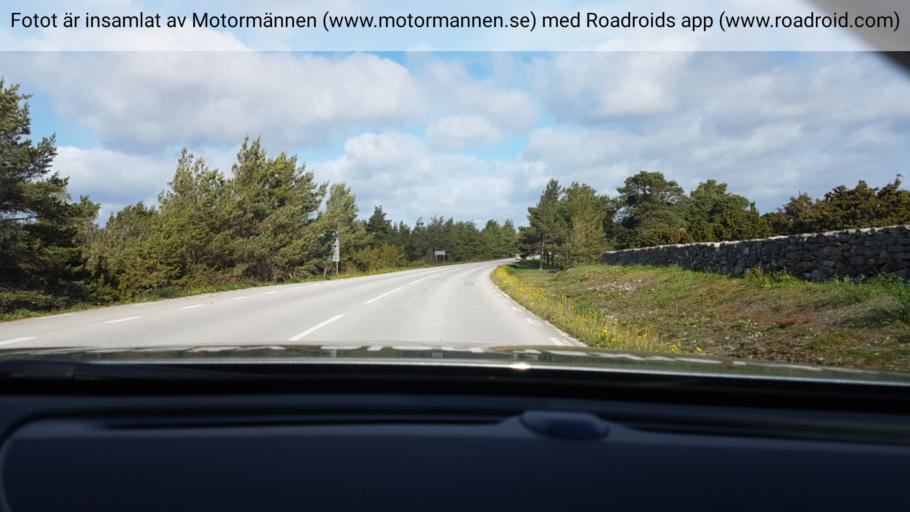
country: SE
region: Gotland
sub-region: Gotland
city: Slite
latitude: 57.8717
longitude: 19.0856
